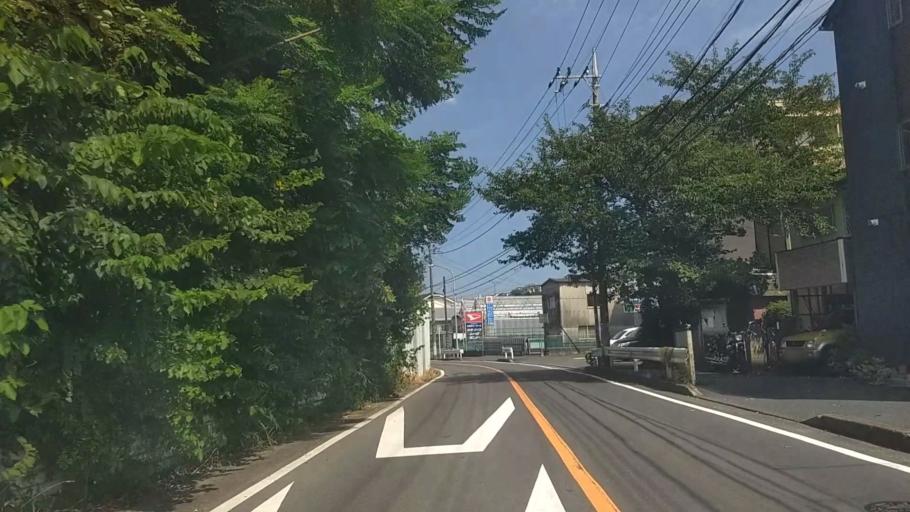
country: JP
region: Kanagawa
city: Yokohama
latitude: 35.4936
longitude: 139.5970
